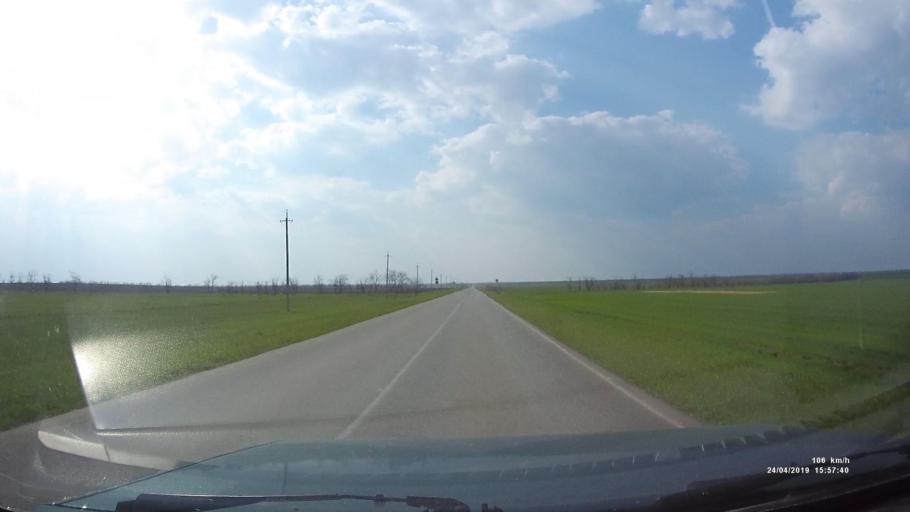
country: RU
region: Kalmykiya
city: Yashalta
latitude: 46.6071
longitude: 42.5042
